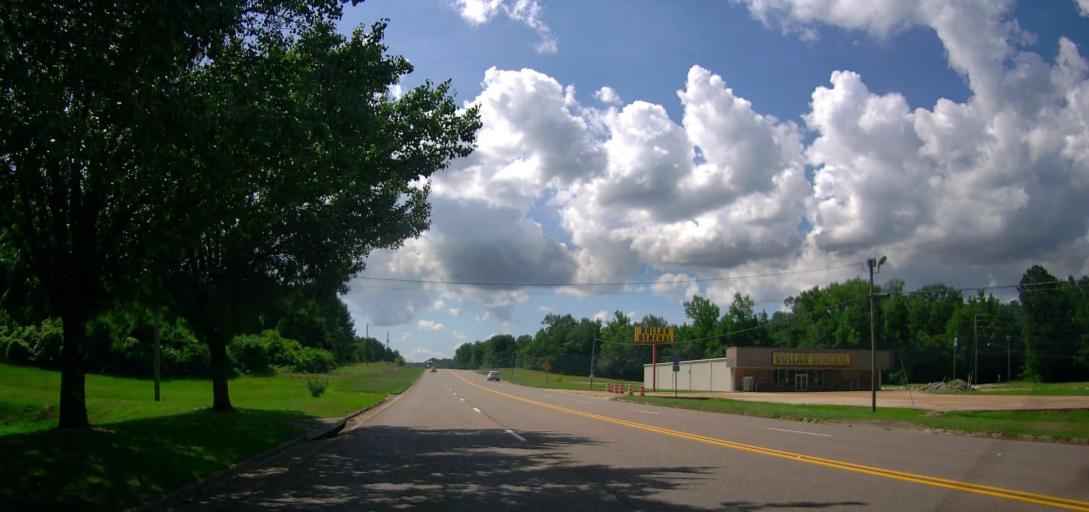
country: US
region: Alabama
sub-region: Pickens County
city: Reform
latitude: 33.3834
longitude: -88.0251
